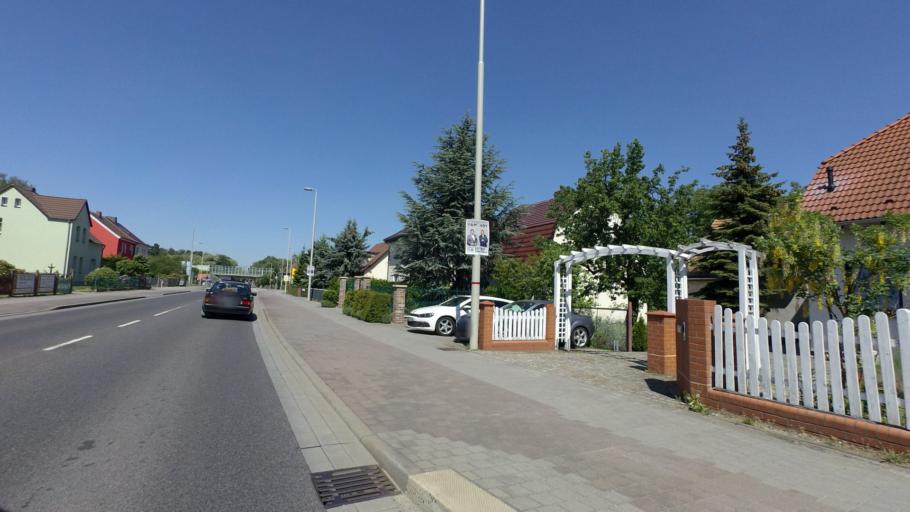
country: DE
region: Brandenburg
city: Cottbus
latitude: 51.7148
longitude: 14.3520
